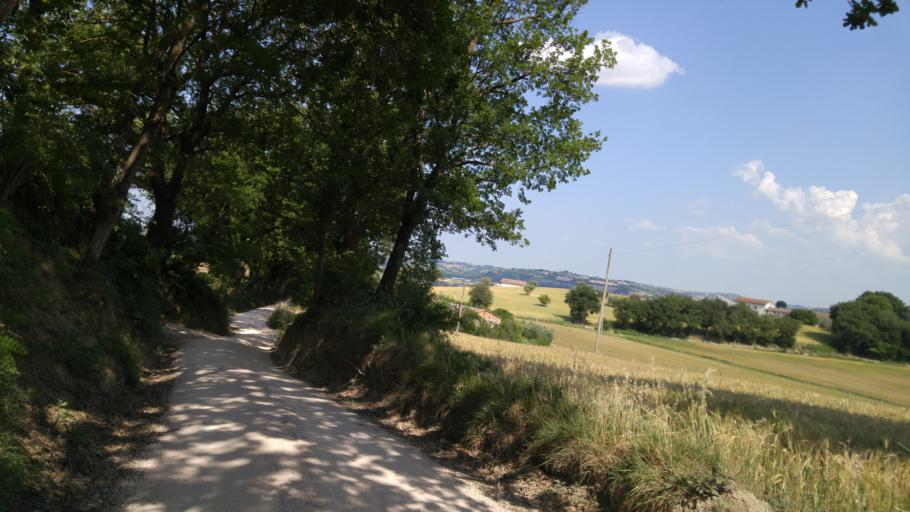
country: IT
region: The Marches
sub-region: Provincia di Pesaro e Urbino
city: Montefelcino
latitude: 43.7276
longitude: 12.8479
